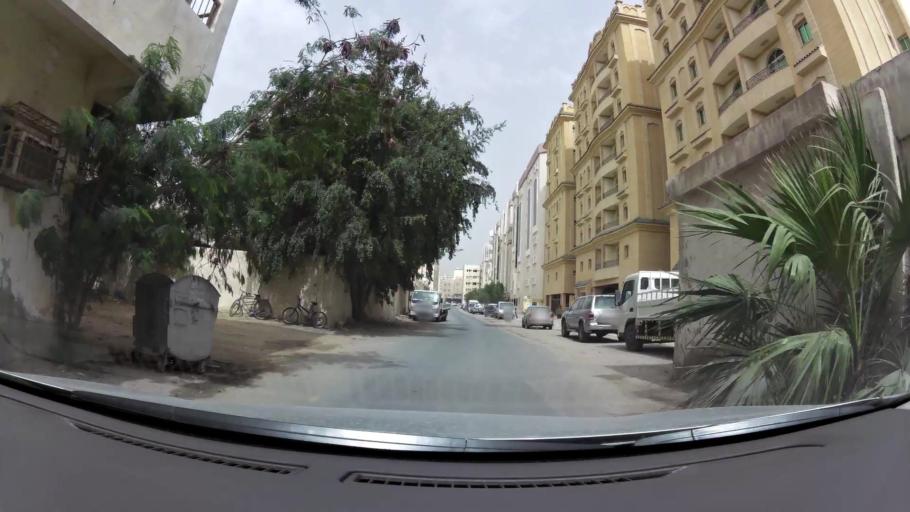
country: QA
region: Baladiyat ad Dawhah
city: Doha
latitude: 25.2692
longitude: 51.5453
